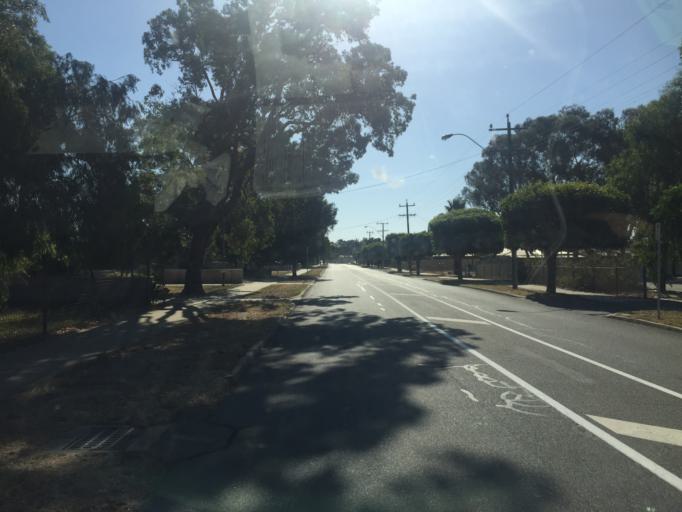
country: AU
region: Western Australia
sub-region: Gosnells
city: Kenwick
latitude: -32.0352
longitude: 115.9734
